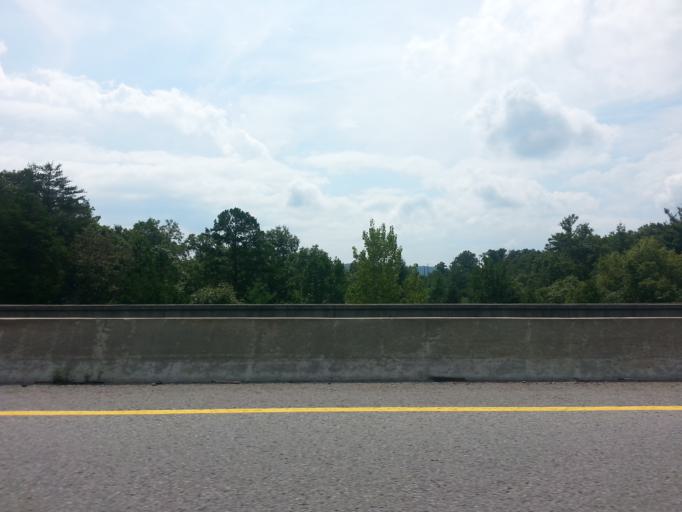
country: US
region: Tennessee
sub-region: Roane County
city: Rockwood
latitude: 35.8955
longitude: -84.7272
